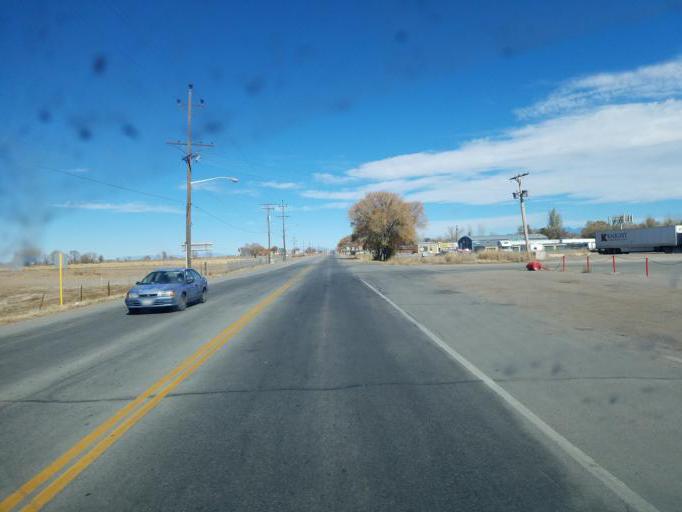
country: US
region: Colorado
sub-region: Alamosa County
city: Alamosa
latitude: 37.4733
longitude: -105.8574
